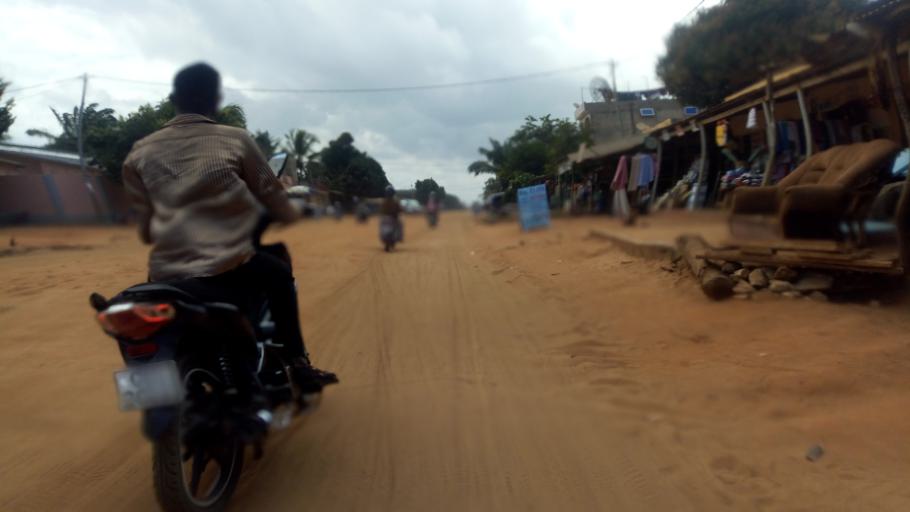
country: TG
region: Maritime
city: Lome
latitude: 6.2236
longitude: 1.1787
